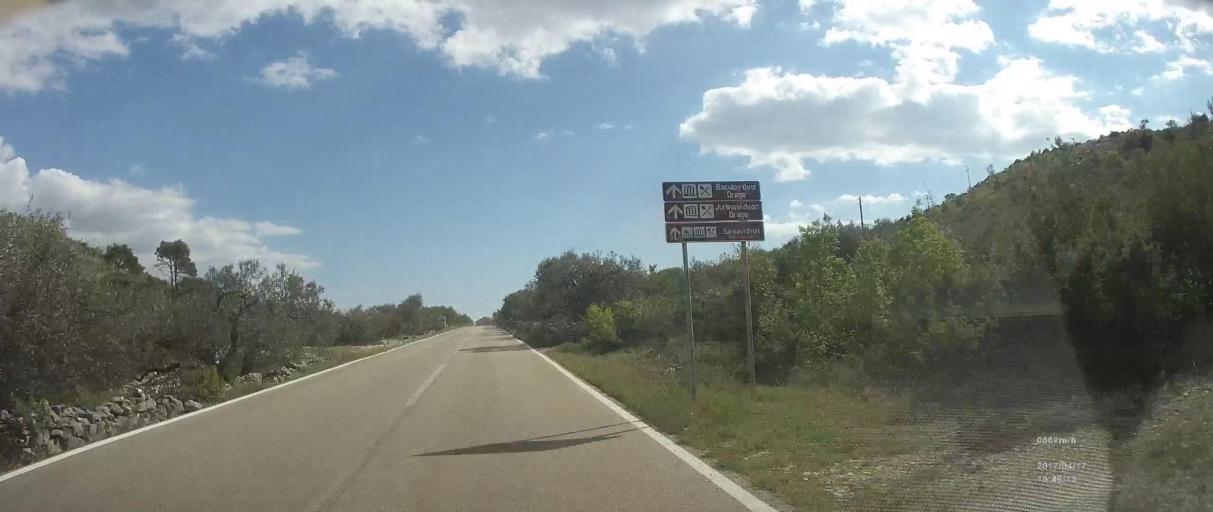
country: HR
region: Sibensko-Kniniska
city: Primosten
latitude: 43.6157
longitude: 15.9763
